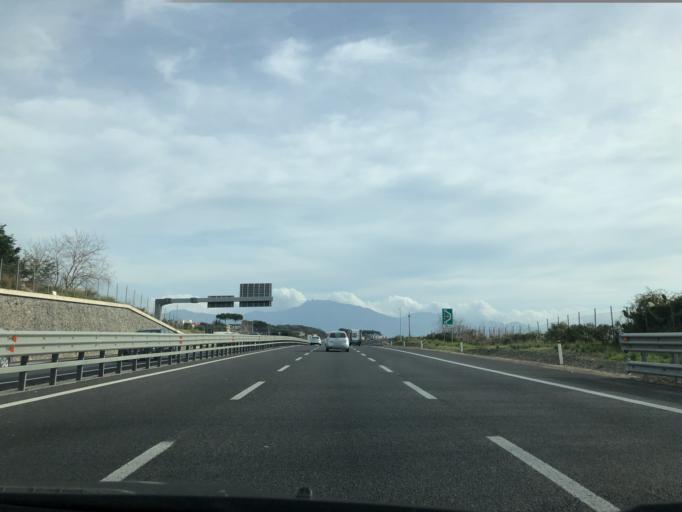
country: IT
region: Campania
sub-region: Provincia di Napoli
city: Ercolano
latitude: 40.8057
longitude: 14.3661
